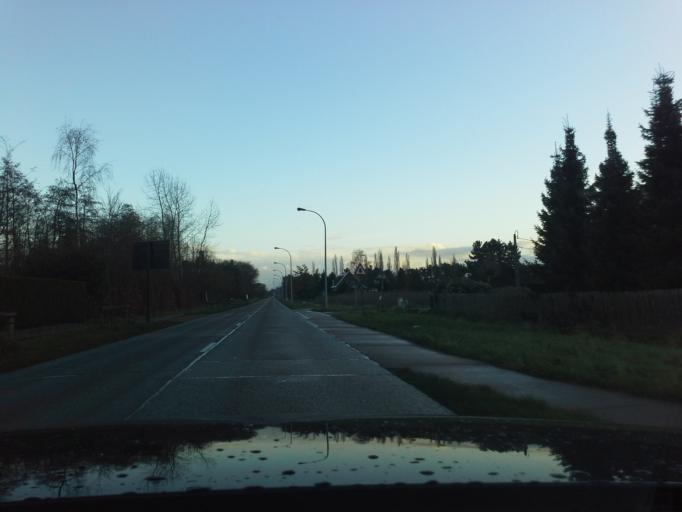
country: BE
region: Flanders
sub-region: Provincie Antwerpen
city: Geel
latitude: 51.1633
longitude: 5.0358
